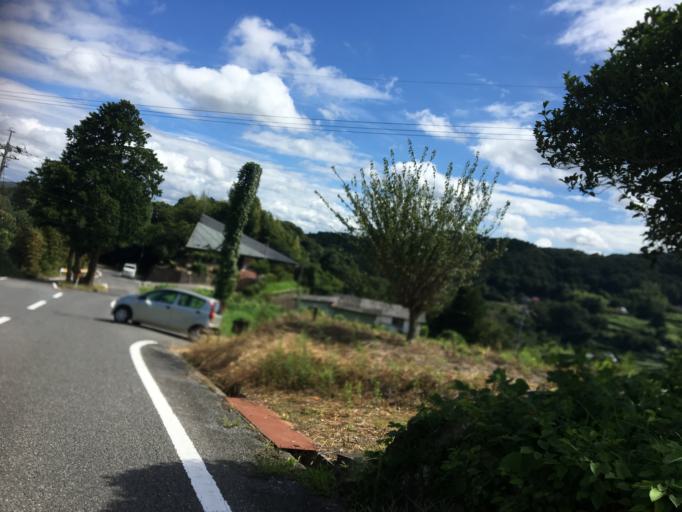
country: JP
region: Okayama
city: Tsuyama
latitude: 34.9008
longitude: 134.1314
